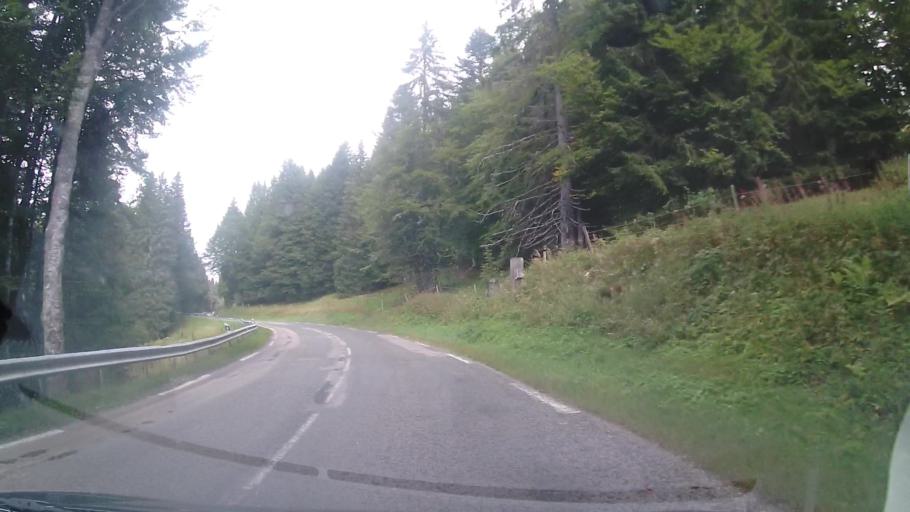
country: FR
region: Franche-Comte
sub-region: Departement du Jura
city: Les Rousses
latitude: 46.4185
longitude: 6.0639
